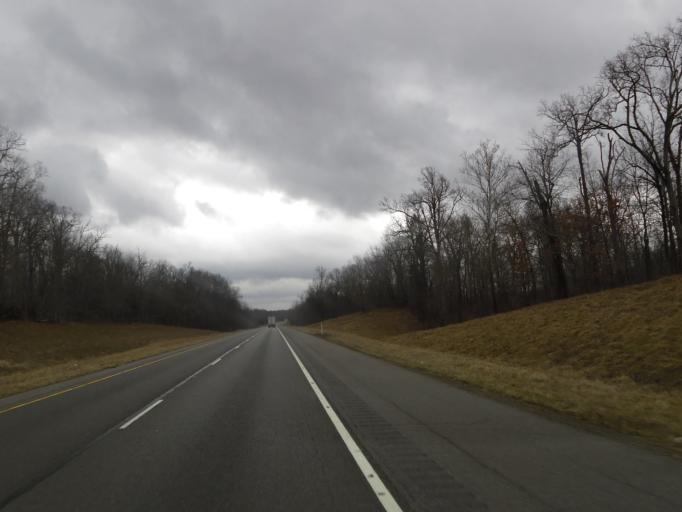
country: US
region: Illinois
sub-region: Massac County
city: Metropolis
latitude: 37.2589
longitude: -88.7289
